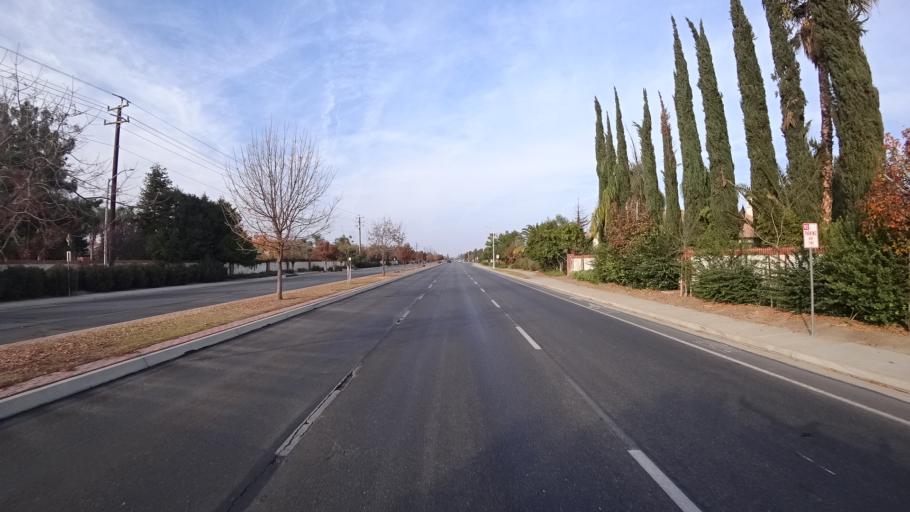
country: US
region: California
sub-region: Kern County
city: Greenacres
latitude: 35.3350
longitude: -119.1279
